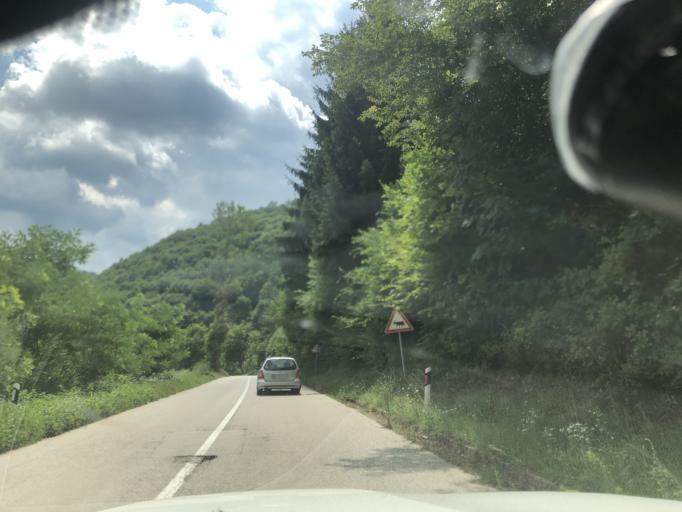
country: RS
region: Central Serbia
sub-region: Jablanicki Okrug
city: Medvega
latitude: 42.7898
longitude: 21.5827
